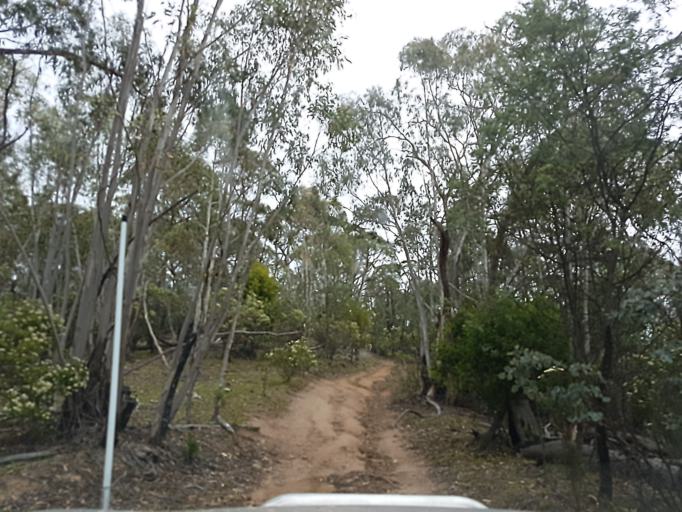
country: AU
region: New South Wales
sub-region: Snowy River
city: Jindabyne
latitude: -36.8747
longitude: 148.3360
